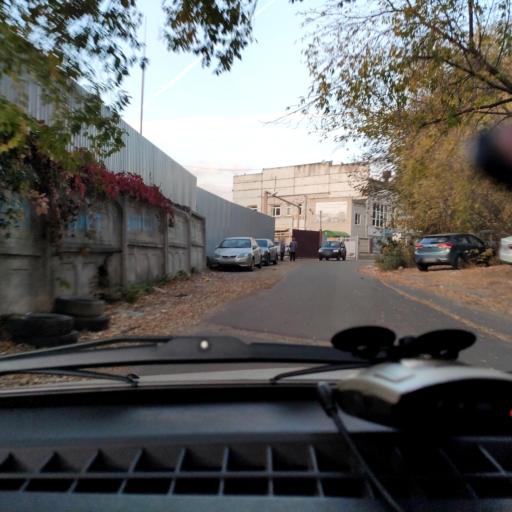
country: RU
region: Voronezj
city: Voronezh
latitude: 51.6605
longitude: 39.1371
